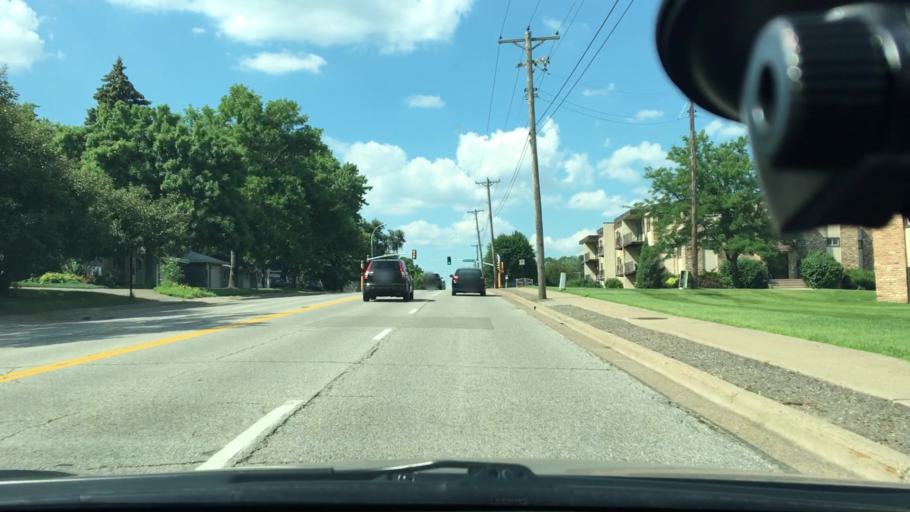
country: US
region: Minnesota
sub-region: Hennepin County
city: New Hope
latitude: 45.0134
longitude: -93.3802
